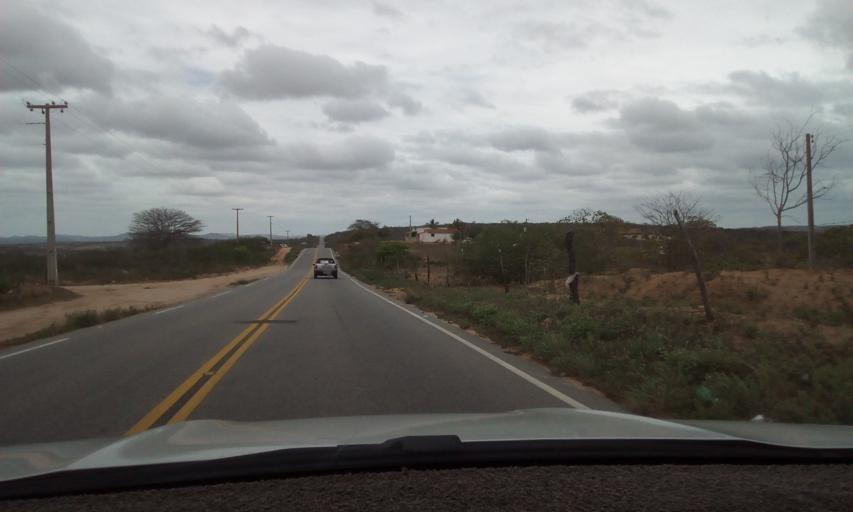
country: BR
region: Paraiba
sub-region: Picui
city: Picui
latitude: -6.5778
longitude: -36.2566
